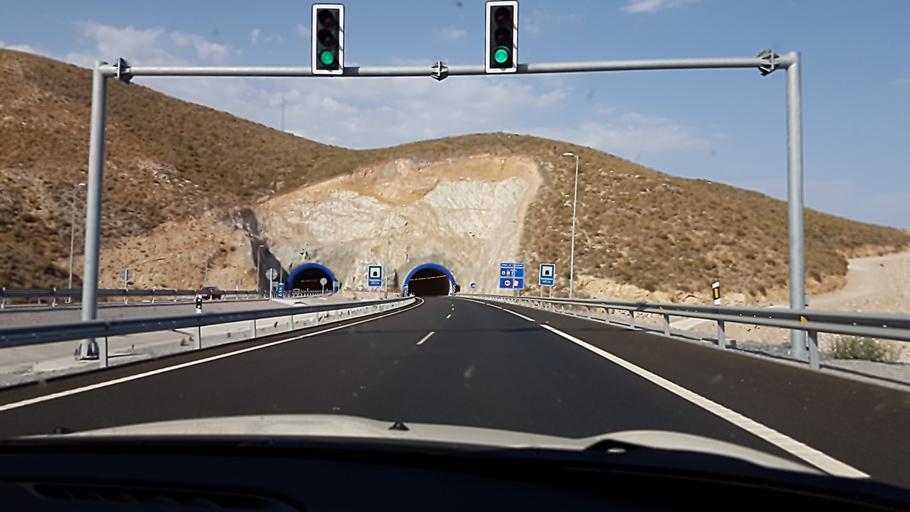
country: ES
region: Andalusia
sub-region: Provincia de Granada
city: Gualchos
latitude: 36.7190
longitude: -3.3775
